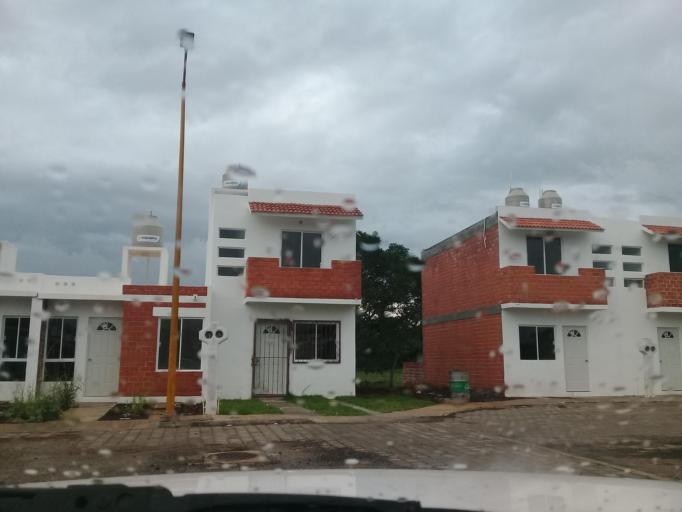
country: MX
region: Veracruz
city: San Andres Tuxtla
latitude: 18.4280
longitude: -95.2190
